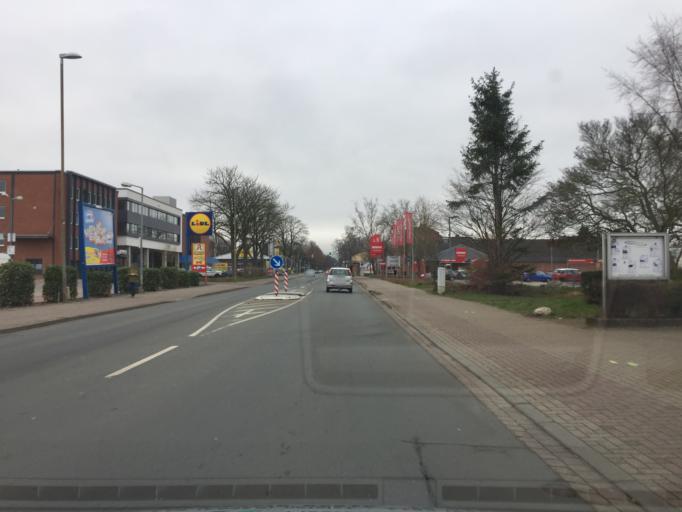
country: DE
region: Lower Saxony
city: Stadthagen
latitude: 52.3249
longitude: 9.1925
